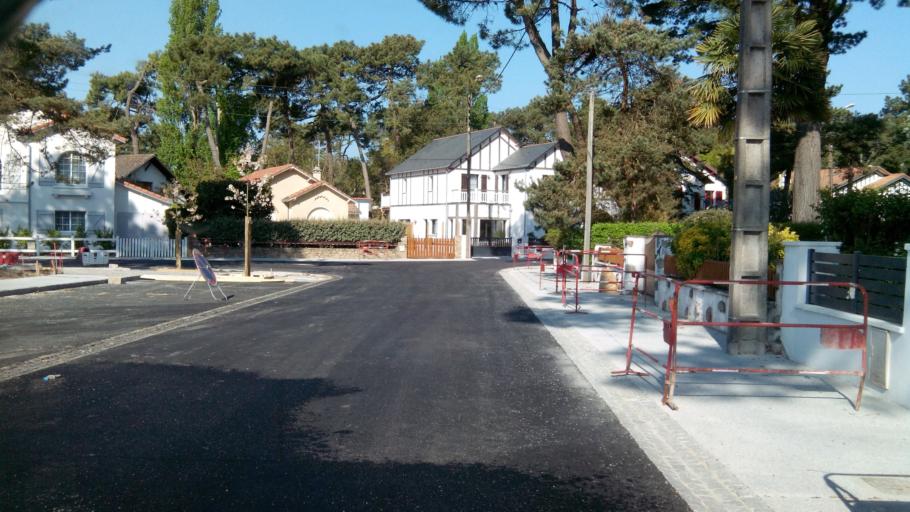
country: FR
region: Pays de la Loire
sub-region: Departement de la Loire-Atlantique
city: La Baule-Escoublac
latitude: 47.2842
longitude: -2.3713
